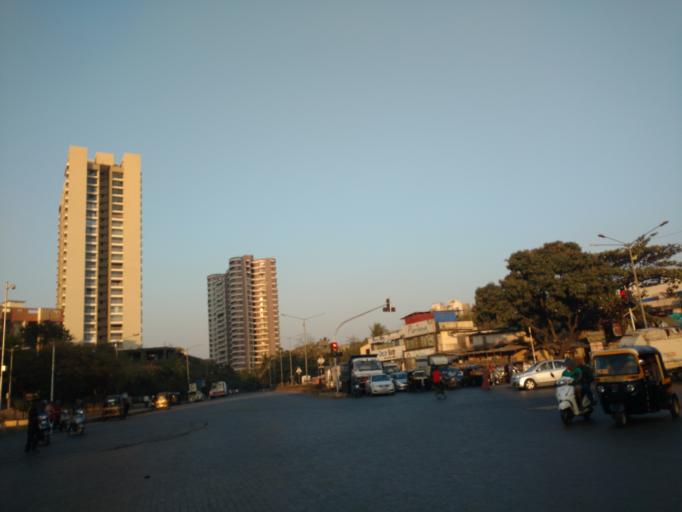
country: IN
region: Maharashtra
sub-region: Mumbai Suburban
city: Borivli
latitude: 19.2150
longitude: 72.8380
